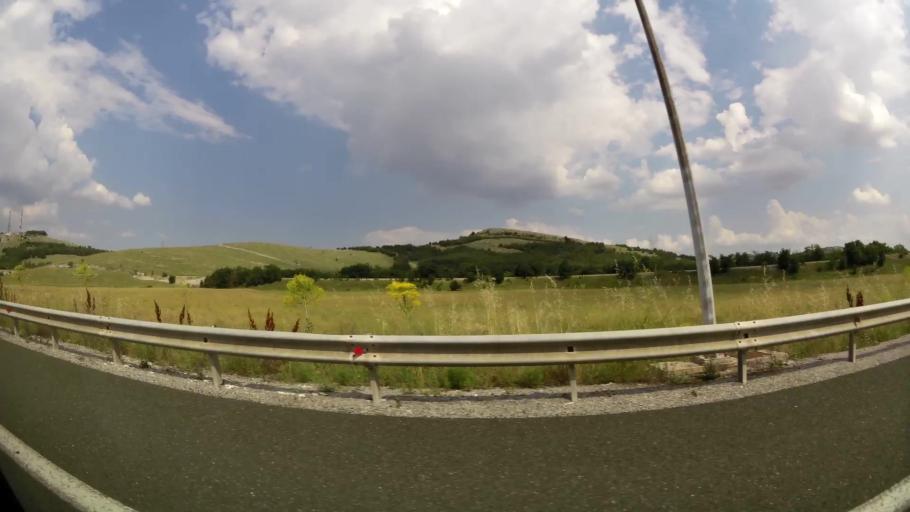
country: GR
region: West Macedonia
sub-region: Nomos Kozanis
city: Koila
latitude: 40.3525
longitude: 21.8105
